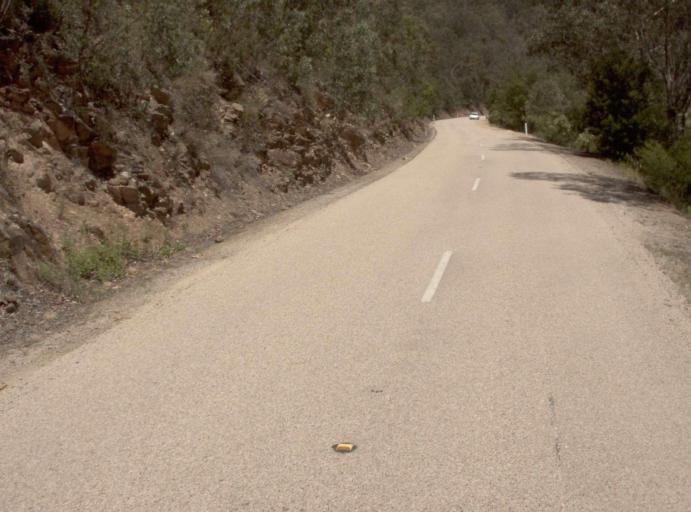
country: AU
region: Victoria
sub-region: East Gippsland
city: Bairnsdale
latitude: -37.4576
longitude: 147.8299
